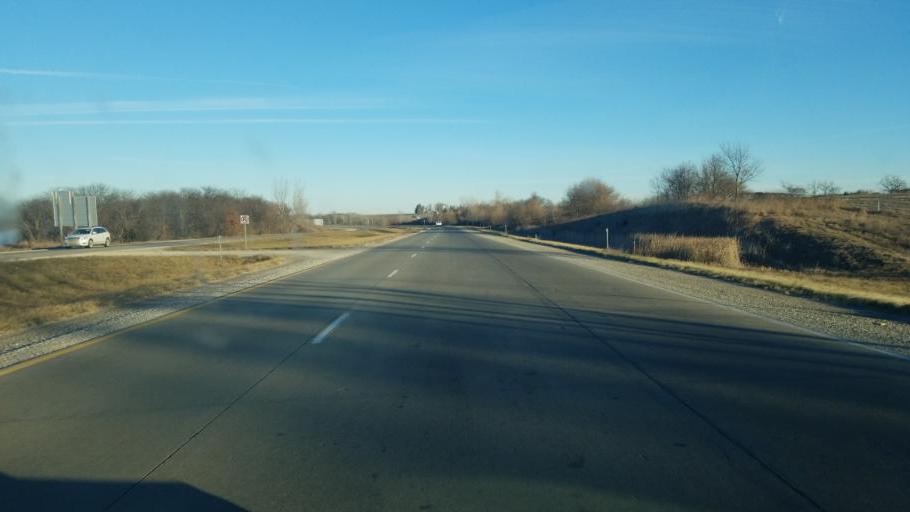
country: US
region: Iowa
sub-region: Mahaska County
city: Oskaloosa
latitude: 41.3015
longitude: -92.6746
